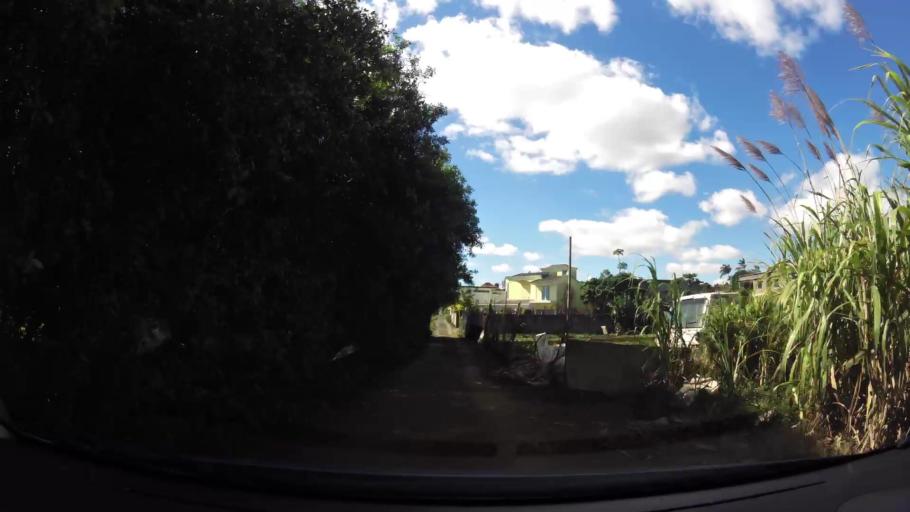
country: MU
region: Plaines Wilhems
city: Vacoas
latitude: -20.2905
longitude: 57.4740
